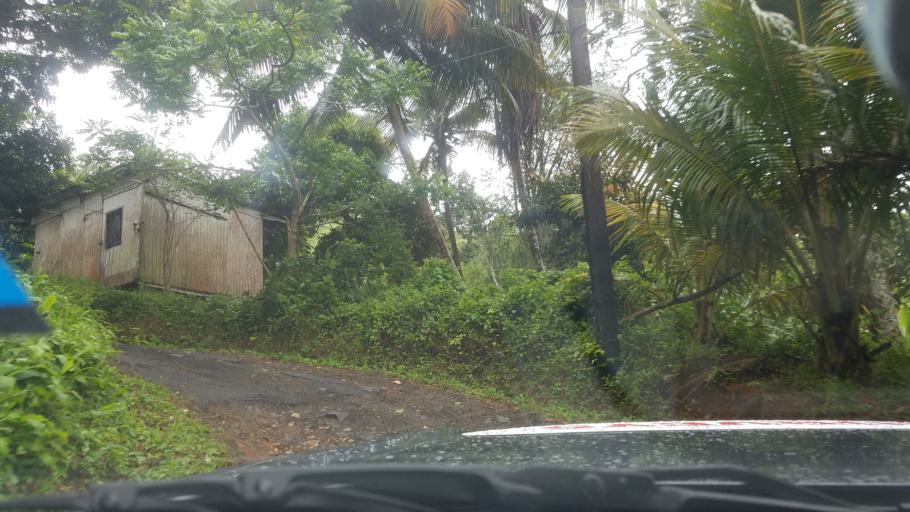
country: LC
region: Castries Quarter
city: Bisee
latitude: 14.0221
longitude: -60.9329
